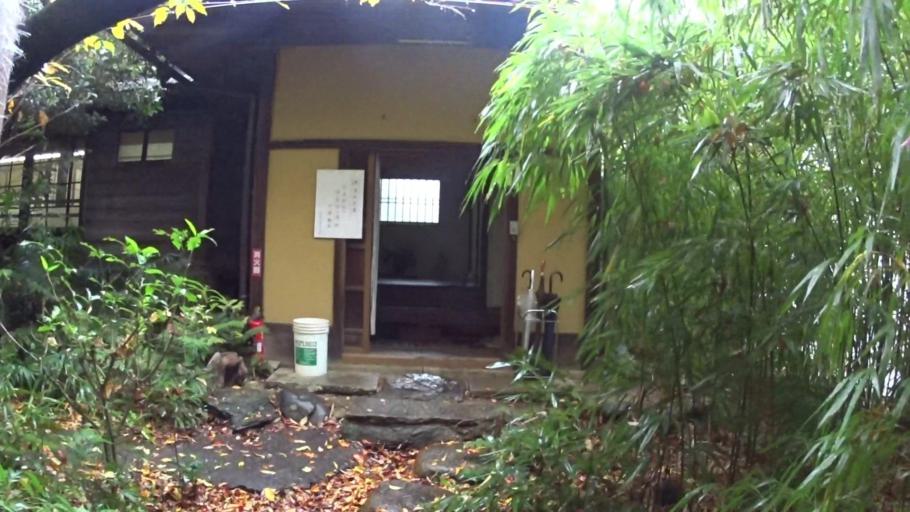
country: JP
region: Kyoto
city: Kyoto
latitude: 35.0300
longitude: 135.7271
